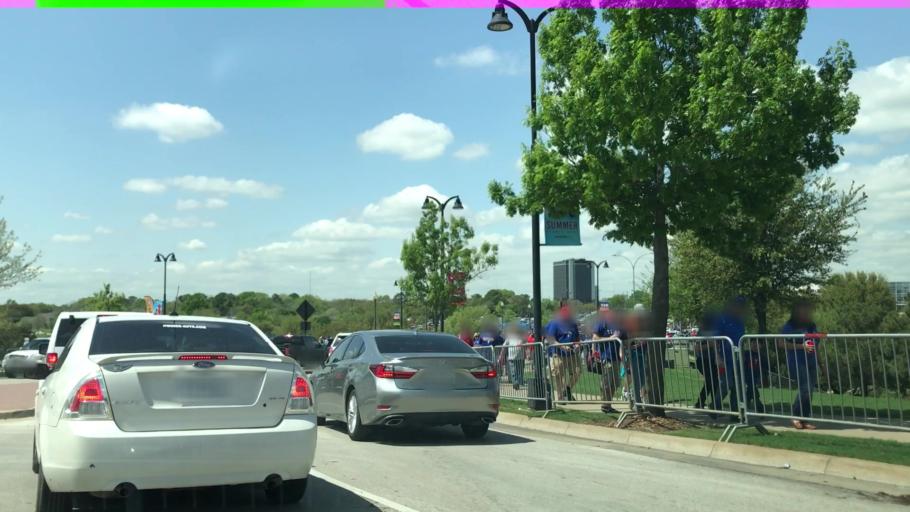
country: US
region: Texas
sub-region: Tarrant County
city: Arlington
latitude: 32.7528
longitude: -97.0840
